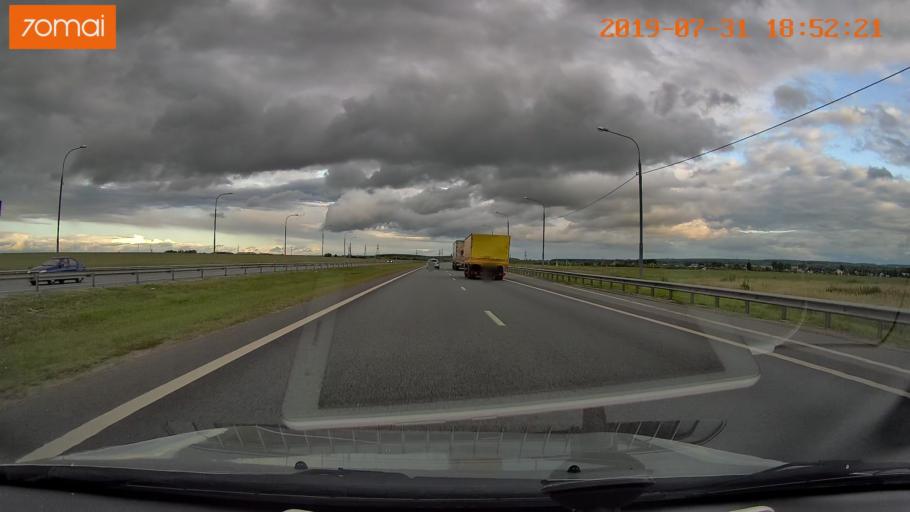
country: RU
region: Moskovskaya
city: Voskresensk
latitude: 55.2146
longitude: 38.6298
